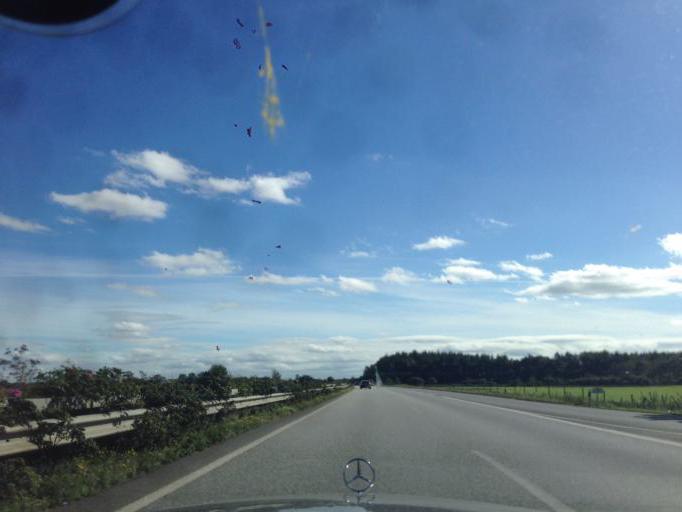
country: DE
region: Schleswig-Holstein
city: Bollingstedt
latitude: 54.6146
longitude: 9.4439
